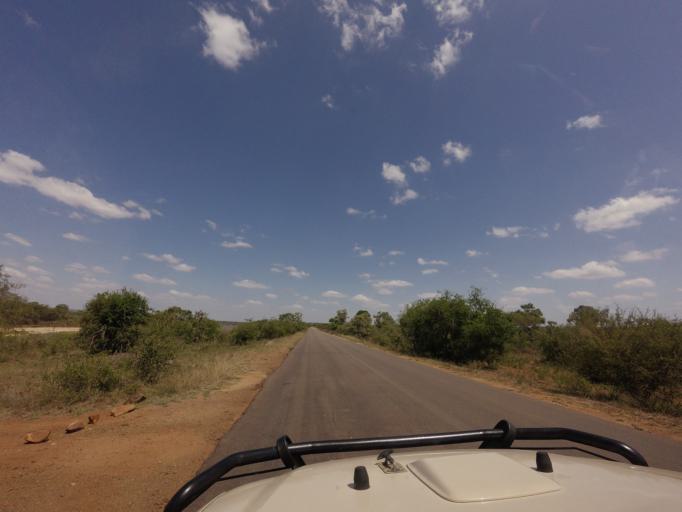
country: ZA
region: Mpumalanga
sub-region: Ehlanzeni District
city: Komatipoort
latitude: -25.1132
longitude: 31.9091
